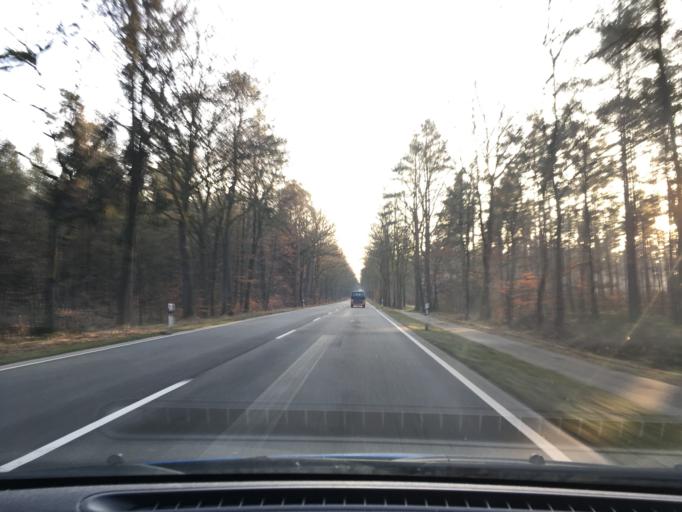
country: DE
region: Lower Saxony
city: Suderburg
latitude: 52.8526
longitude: 10.4905
